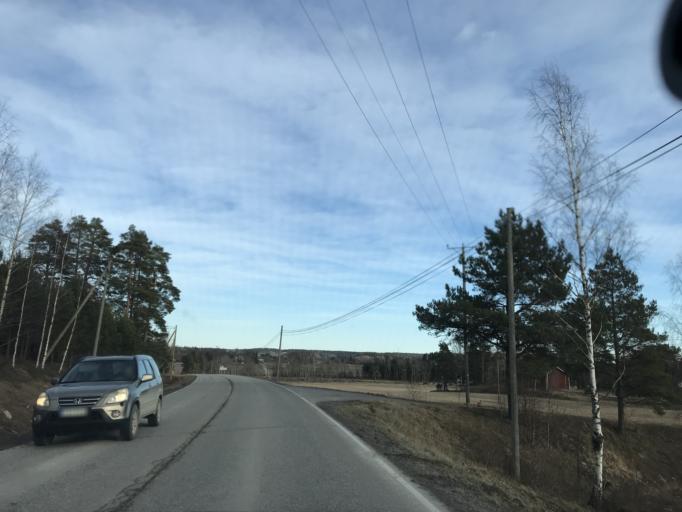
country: FI
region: Uusimaa
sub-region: Raaseporin
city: Pohja
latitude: 60.0913
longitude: 23.4878
